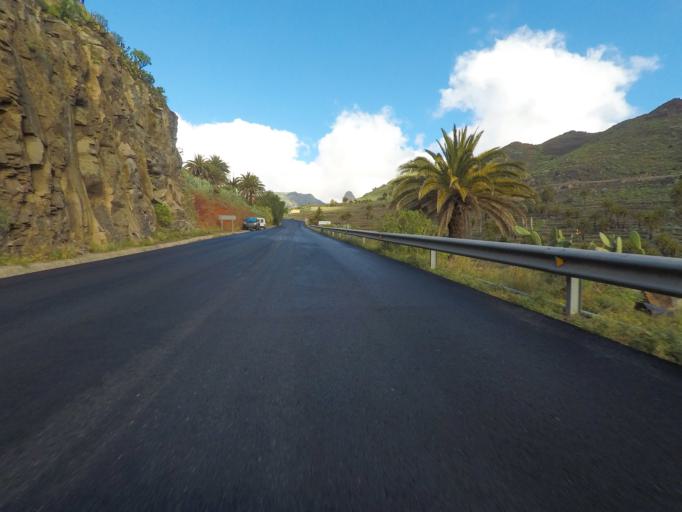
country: ES
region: Canary Islands
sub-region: Provincia de Santa Cruz de Tenerife
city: Alajero
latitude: 28.0742
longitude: -17.2074
